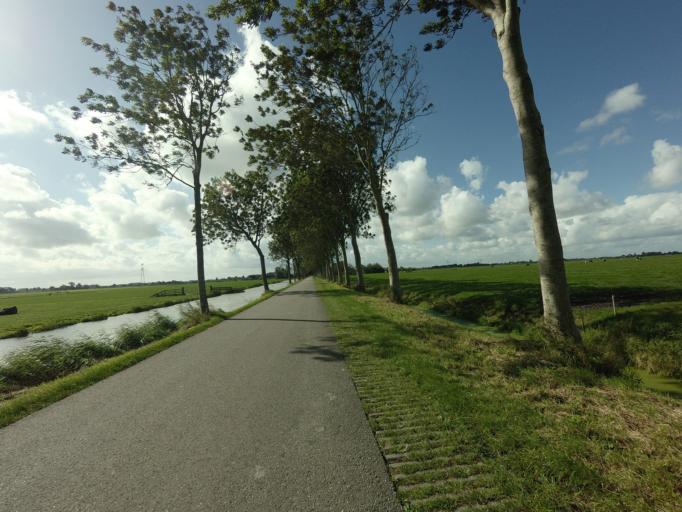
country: NL
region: North Holland
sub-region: Gemeente Hoorn
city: Hoorn
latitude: 52.6630
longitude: 5.0027
